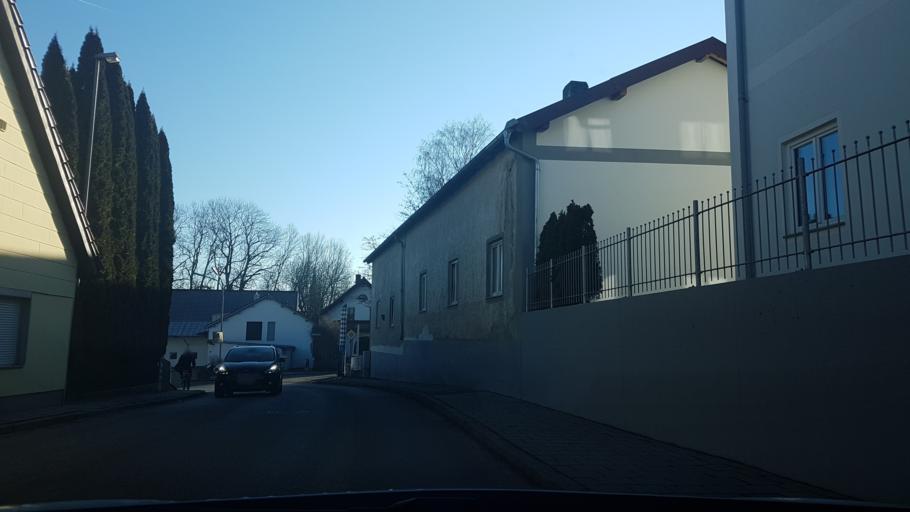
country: DE
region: Bavaria
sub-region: Upper Bavaria
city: Stammham
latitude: 48.3074
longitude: 11.8650
